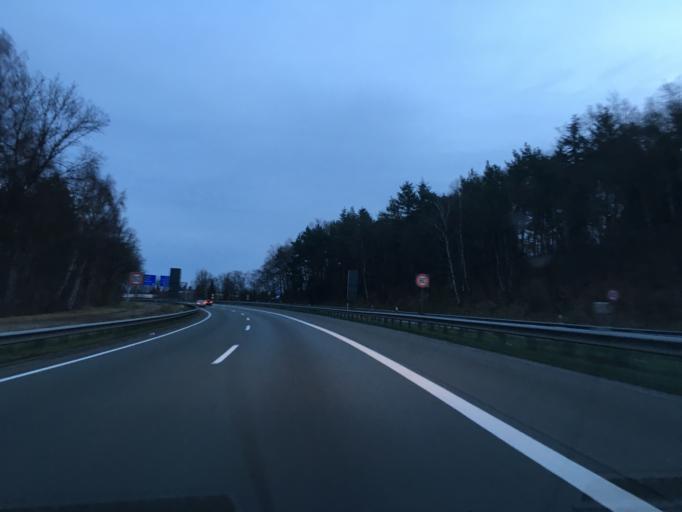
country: DE
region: Lower Saxony
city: Harmstorf
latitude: 53.3811
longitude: 10.0190
